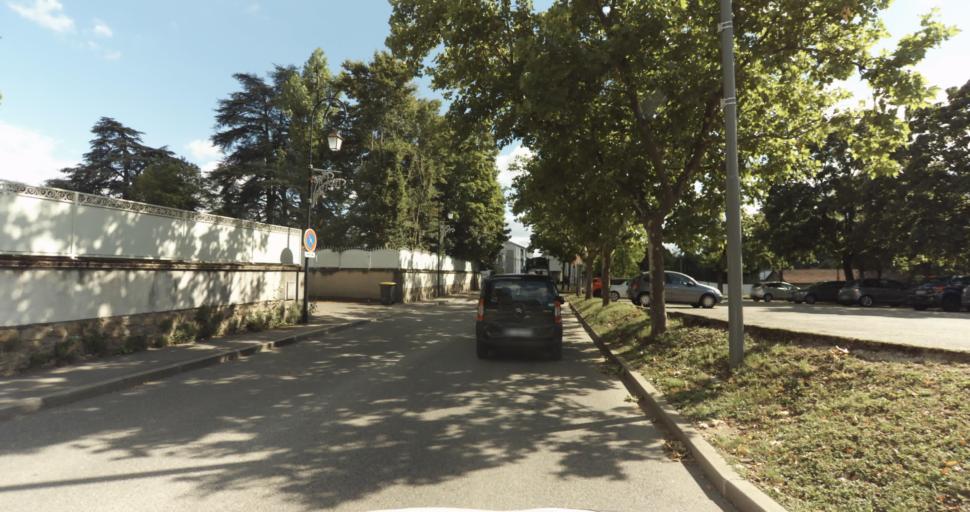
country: FR
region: Rhone-Alpes
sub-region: Departement du Rhone
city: Chaponost
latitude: 45.7096
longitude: 4.7460
